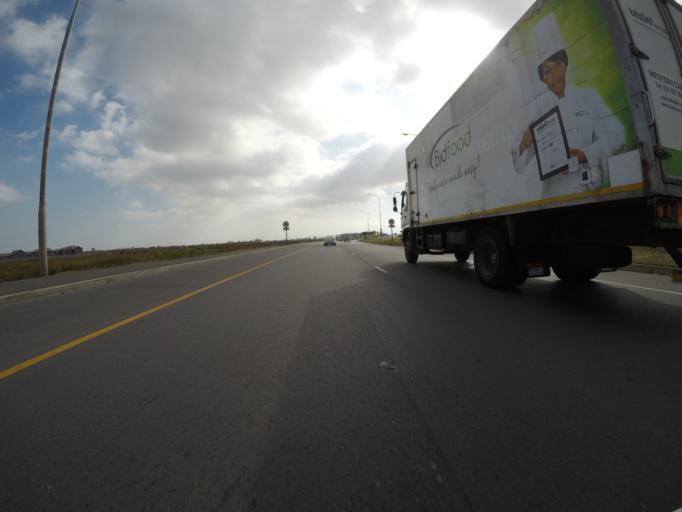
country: ZA
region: Western Cape
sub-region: City of Cape Town
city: Kraaifontein
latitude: -33.9563
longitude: 18.6862
